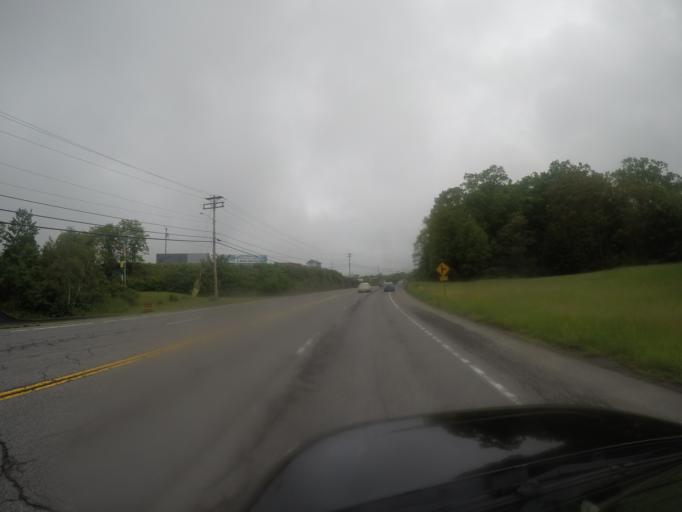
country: US
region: New York
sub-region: Ulster County
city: West Hurley
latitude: 41.9792
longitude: -74.0855
